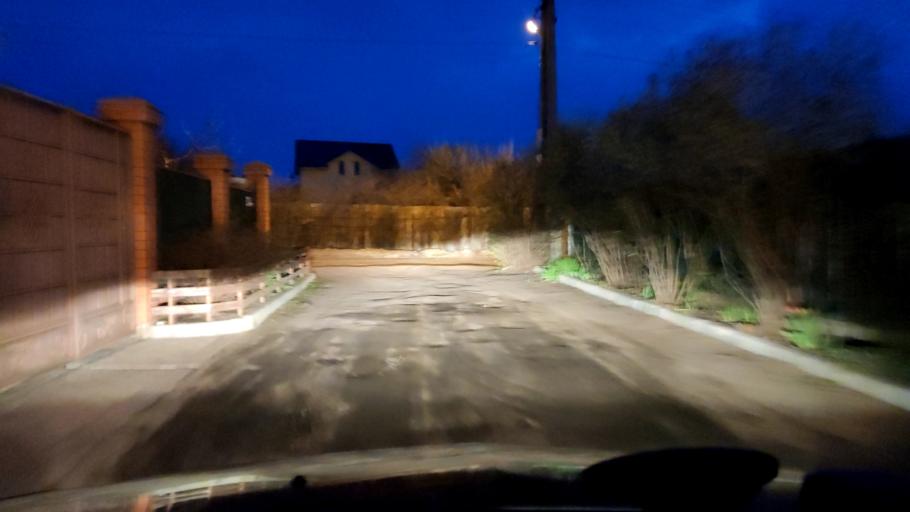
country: RU
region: Voronezj
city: Pridonskoy
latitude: 51.6309
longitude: 39.1018
